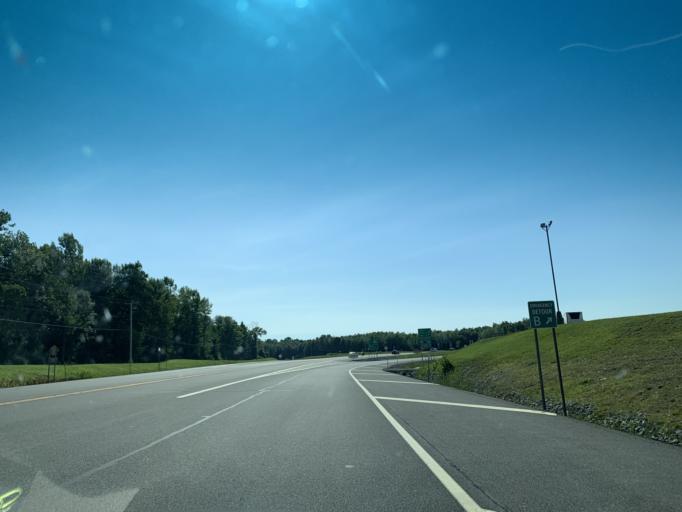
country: US
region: New York
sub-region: Oneida County
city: Sherrill
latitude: 43.1205
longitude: -75.5881
